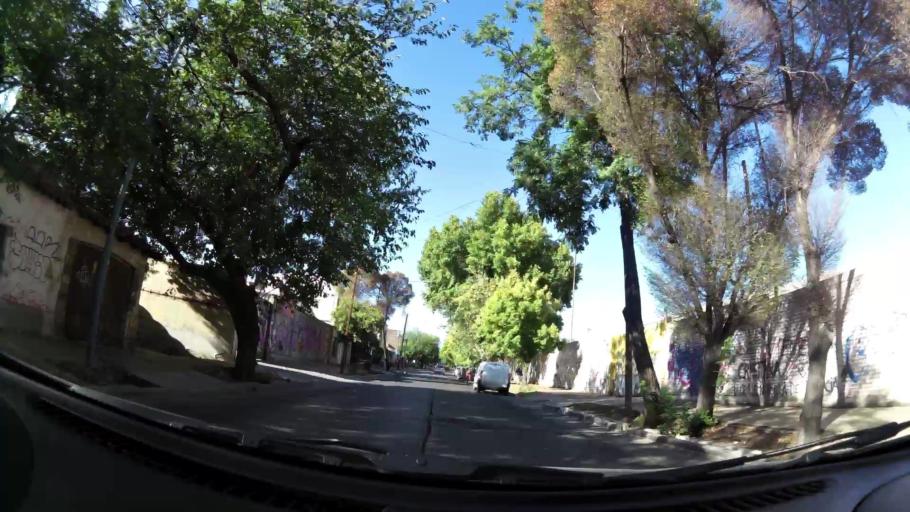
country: AR
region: Mendoza
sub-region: Departamento de Godoy Cruz
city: Godoy Cruz
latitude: -32.9334
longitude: -68.8476
